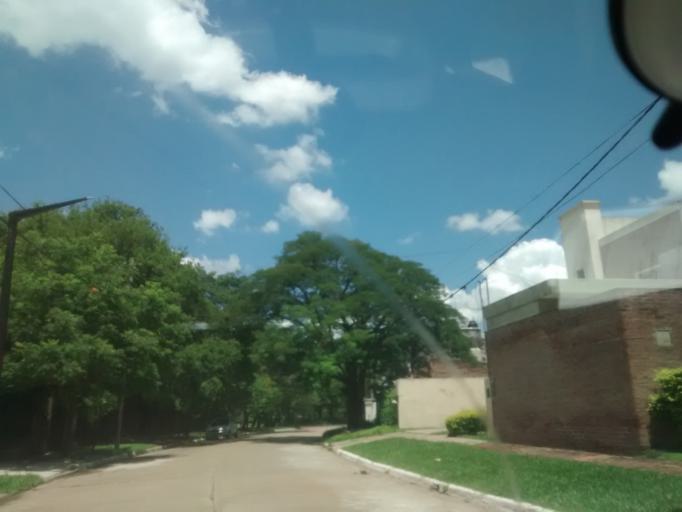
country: AR
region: Chaco
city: Resistencia
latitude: -27.4334
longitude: -58.9809
